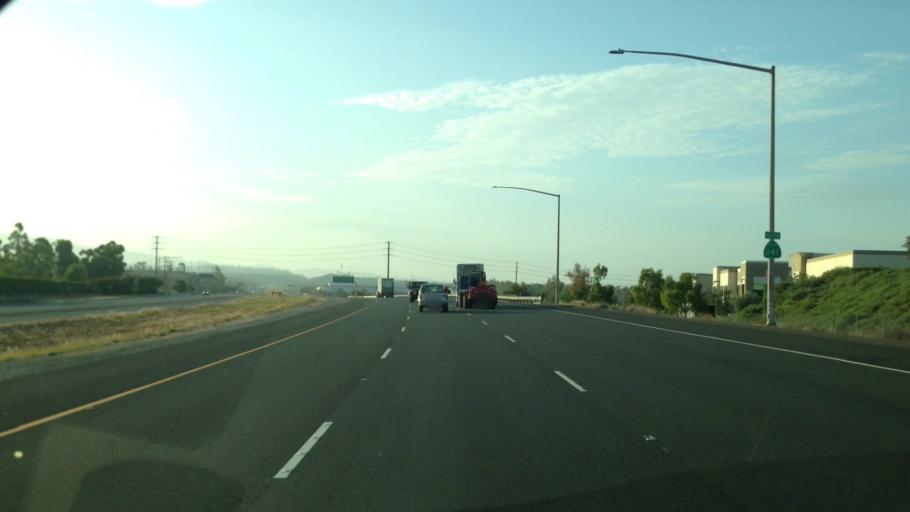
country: US
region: California
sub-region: Orange County
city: Foothill Ranch
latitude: 33.6752
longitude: -117.6691
